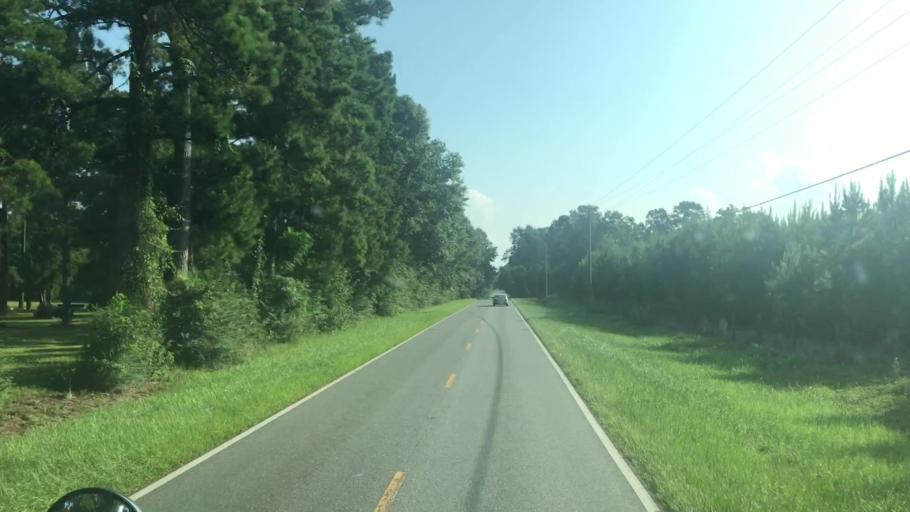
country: US
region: Florida
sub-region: Gadsden County
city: Quincy
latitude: 30.6418
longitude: -84.5741
